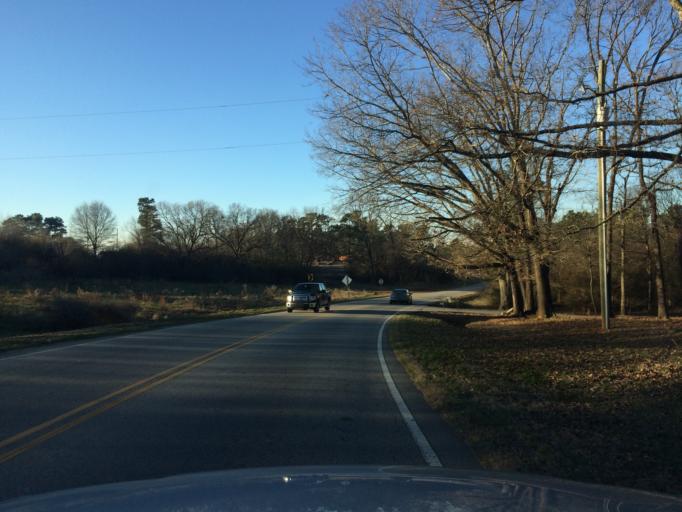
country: US
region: Georgia
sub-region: Barrow County
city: Winder
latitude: 33.9491
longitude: -83.7670
